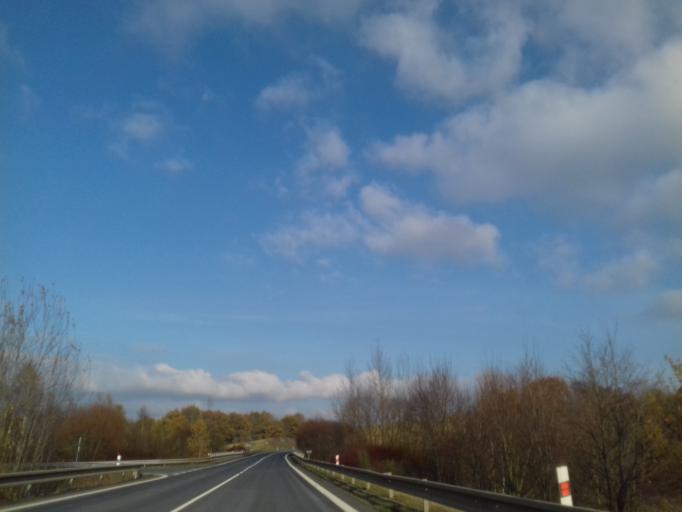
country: CZ
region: Plzensky
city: Meclov
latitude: 49.5150
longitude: 12.9120
